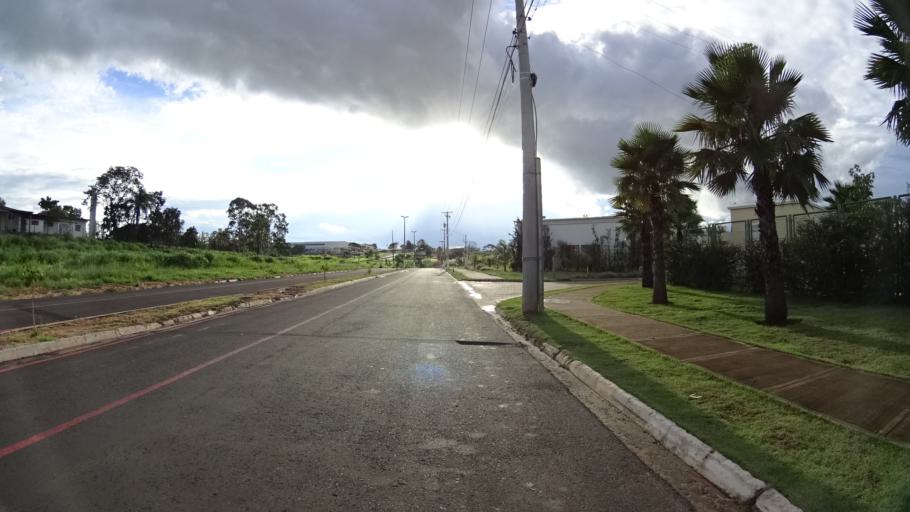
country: BR
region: Sao Paulo
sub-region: Marilia
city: Marilia
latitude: -22.2266
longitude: -49.9041
